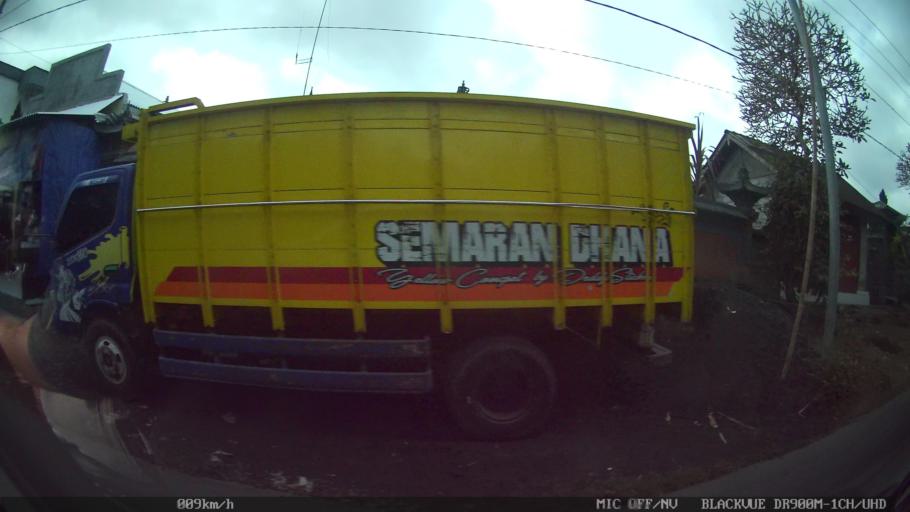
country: ID
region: Bali
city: Banjar Susut Kaja
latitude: -8.4359
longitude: 115.3222
